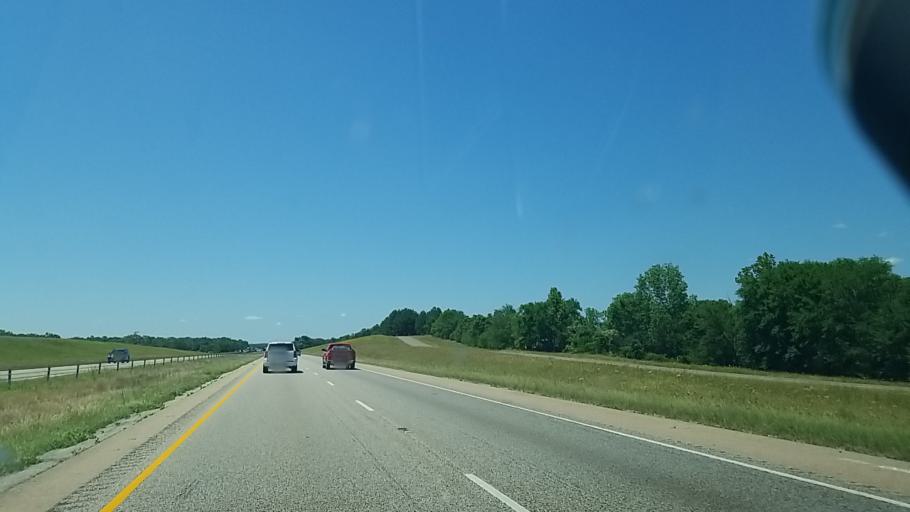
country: US
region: Texas
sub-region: Leon County
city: Buffalo
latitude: 31.3899
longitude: -96.0282
